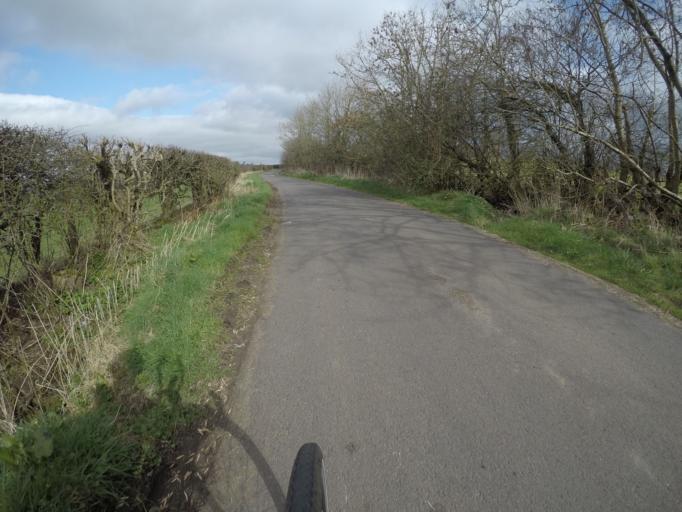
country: GB
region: Scotland
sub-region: North Ayrshire
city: Irvine
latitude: 55.6382
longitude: -4.6300
